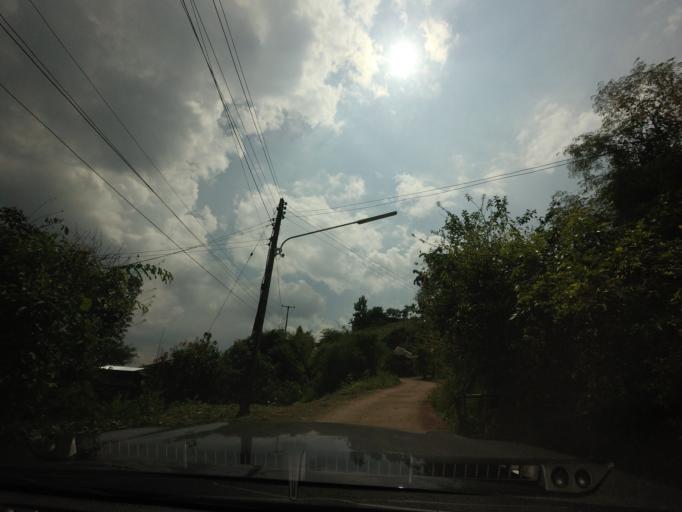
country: TH
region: Nan
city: Bo Kluea
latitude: 19.1908
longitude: 101.2004
